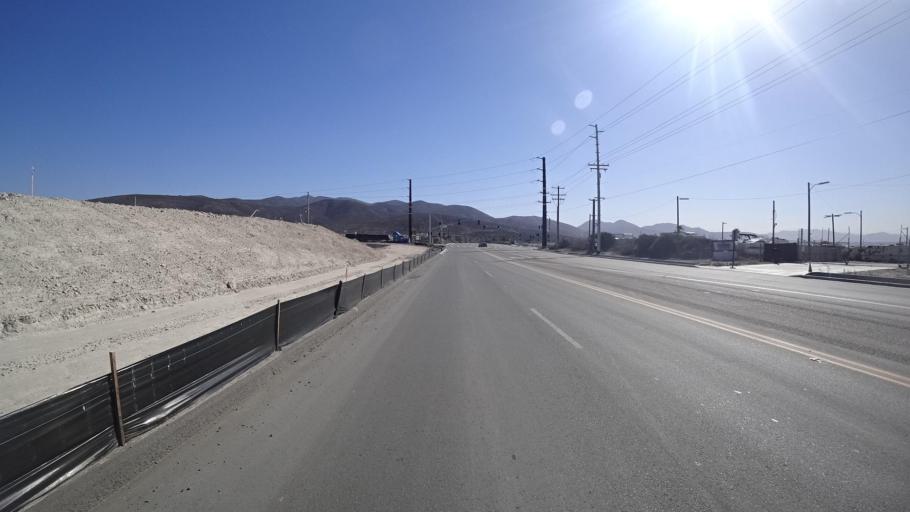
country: MX
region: Baja California
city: Tijuana
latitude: 32.5675
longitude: -116.9204
